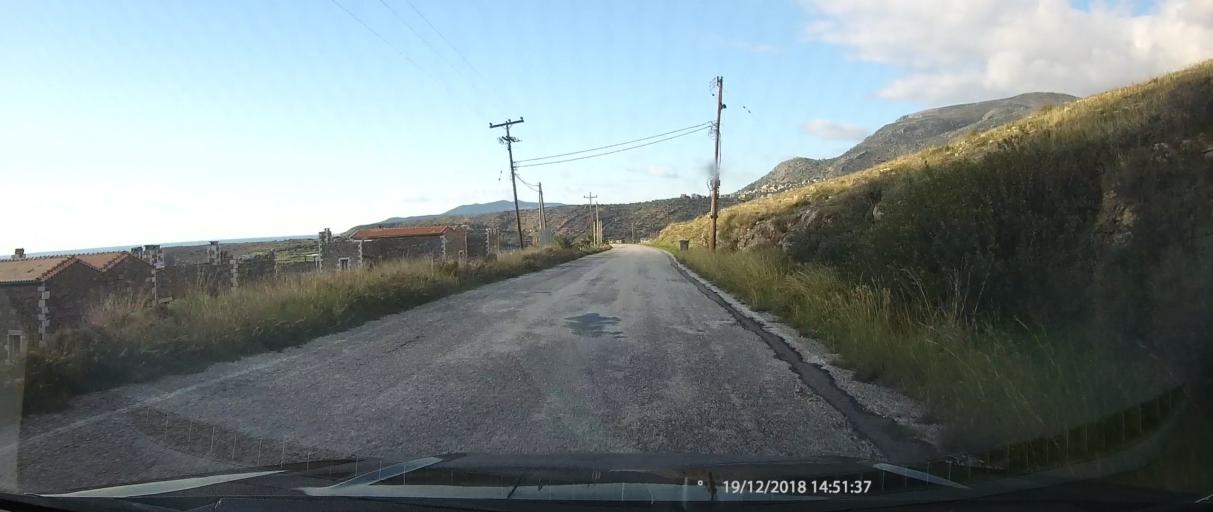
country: GR
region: Peloponnese
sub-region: Nomos Lakonias
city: Gytheio
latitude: 36.4588
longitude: 22.4465
